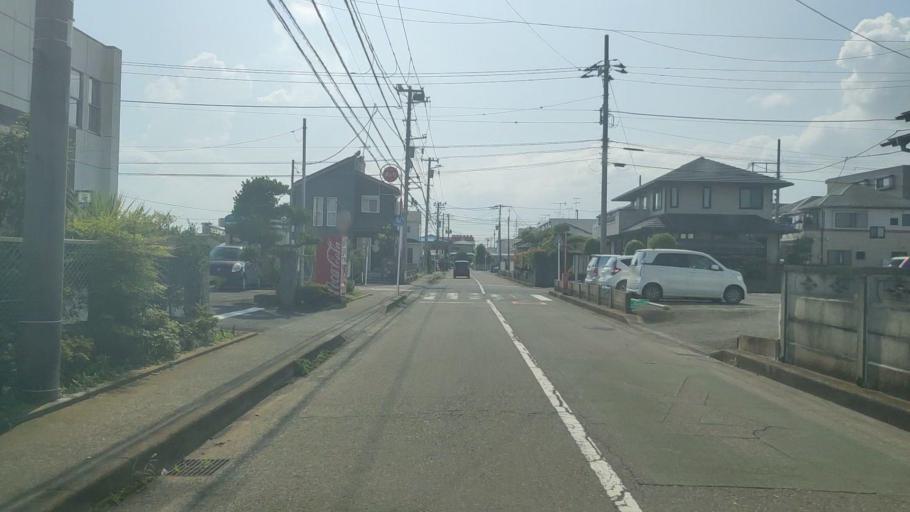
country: JP
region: Kanagawa
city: Hiratsuka
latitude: 35.3565
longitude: 139.3296
